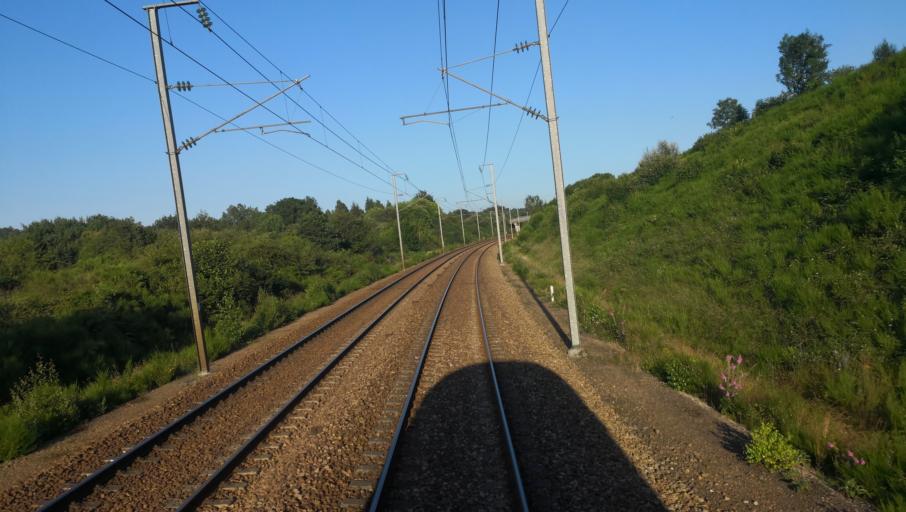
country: FR
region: Lower Normandy
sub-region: Departement du Calvados
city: Beuvillers
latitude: 49.1215
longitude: 0.3306
